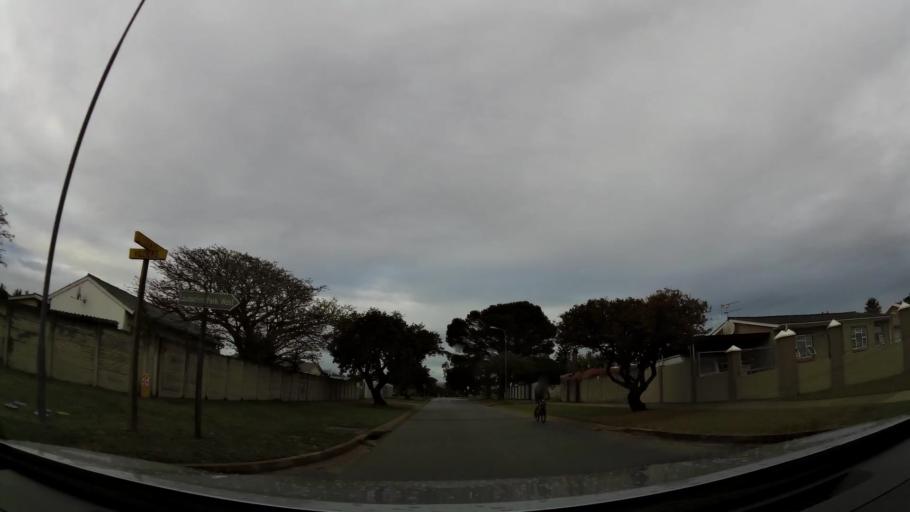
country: ZA
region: Eastern Cape
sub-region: Nelson Mandela Bay Metropolitan Municipality
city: Port Elizabeth
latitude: -33.9835
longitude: 25.5587
